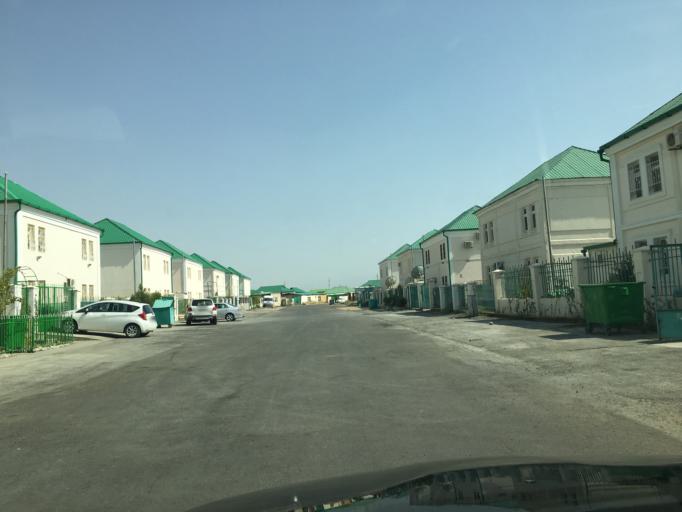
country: TM
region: Ahal
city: Ashgabat
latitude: 38.0000
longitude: 58.3982
